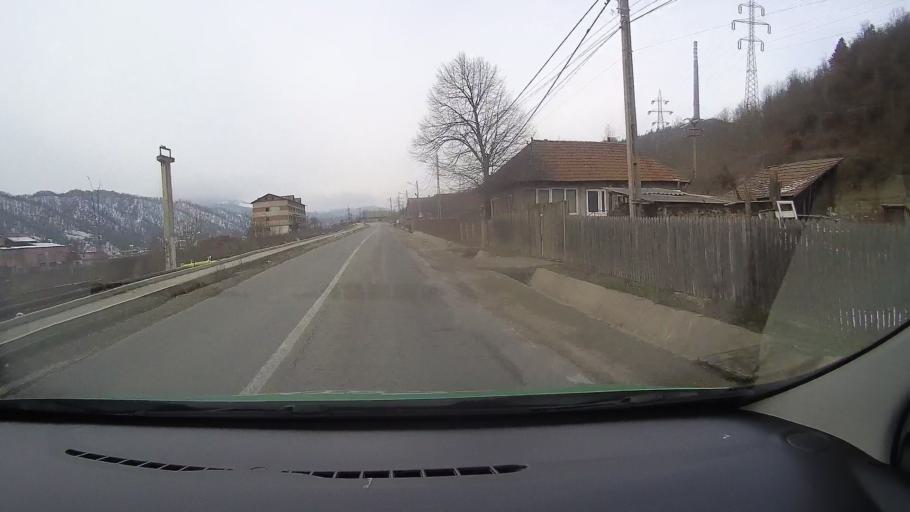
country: RO
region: Alba
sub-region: Oras Zlatna
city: Zlatna
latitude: 46.1060
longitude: 23.2407
